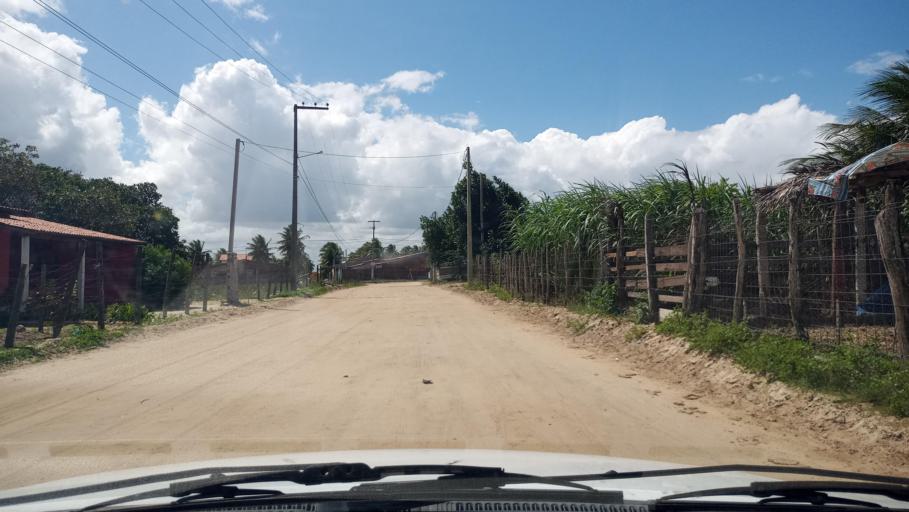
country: BR
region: Rio Grande do Norte
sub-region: Brejinho
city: Brejinho
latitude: -6.1938
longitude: -35.3641
